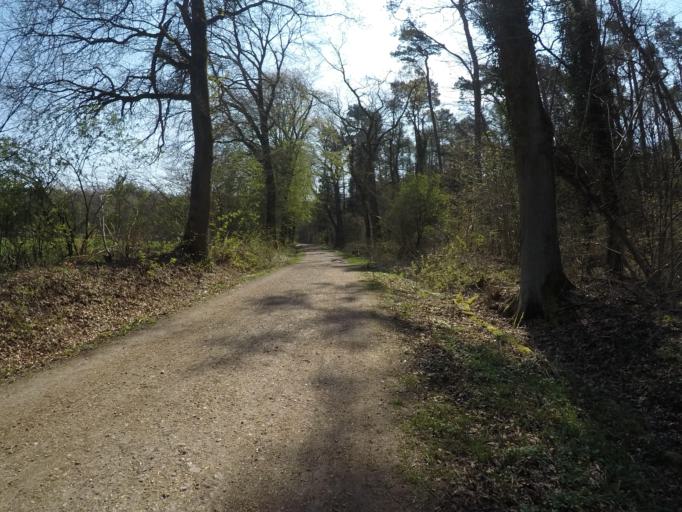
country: DE
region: Schleswig-Holstein
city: Rellingen
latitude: 53.6096
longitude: 9.7898
